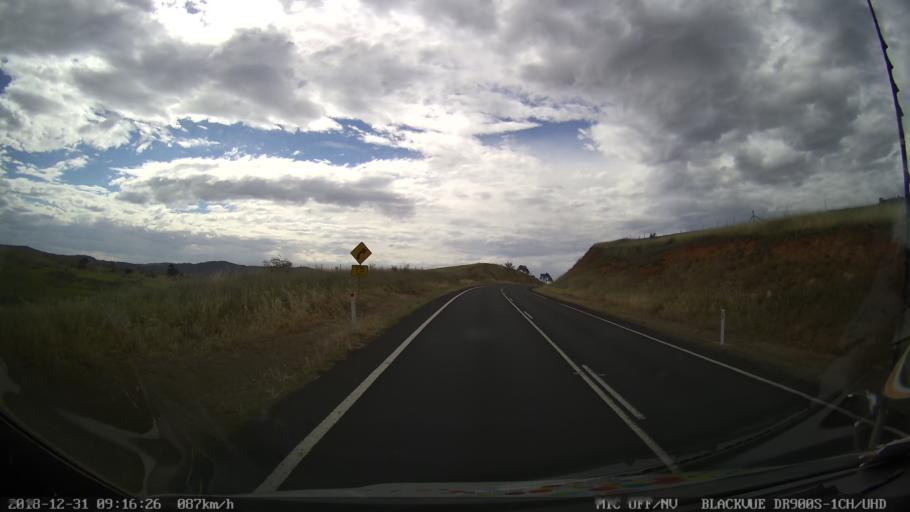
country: AU
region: New South Wales
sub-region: Snowy River
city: Jindabyne
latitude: -36.3957
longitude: 148.5960
